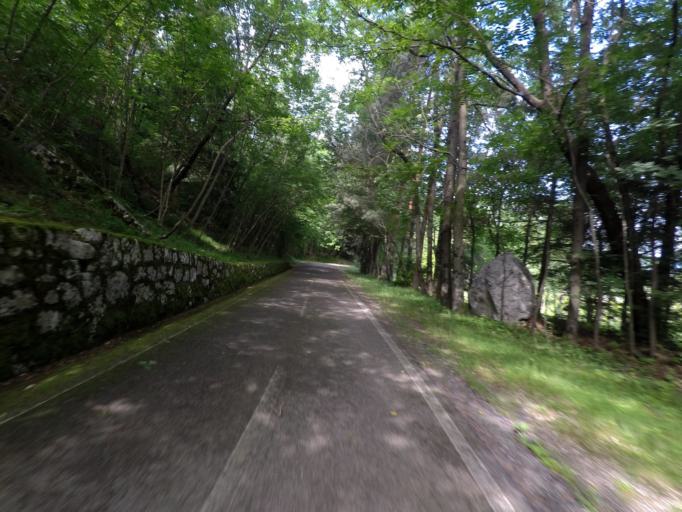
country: IT
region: Friuli Venezia Giulia
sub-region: Provincia di Udine
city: Amaro
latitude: 46.3606
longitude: 13.0862
